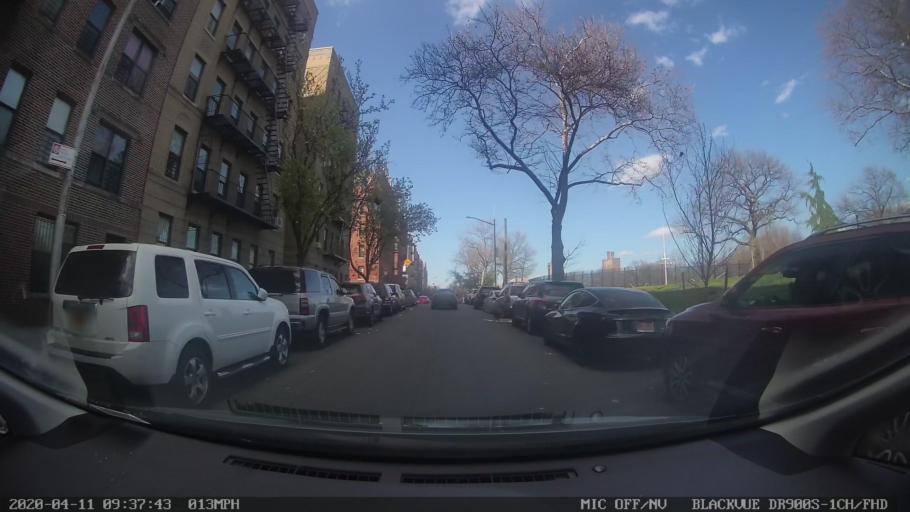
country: US
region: New York
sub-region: Bronx
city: The Bronx
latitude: 40.8389
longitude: -73.8993
